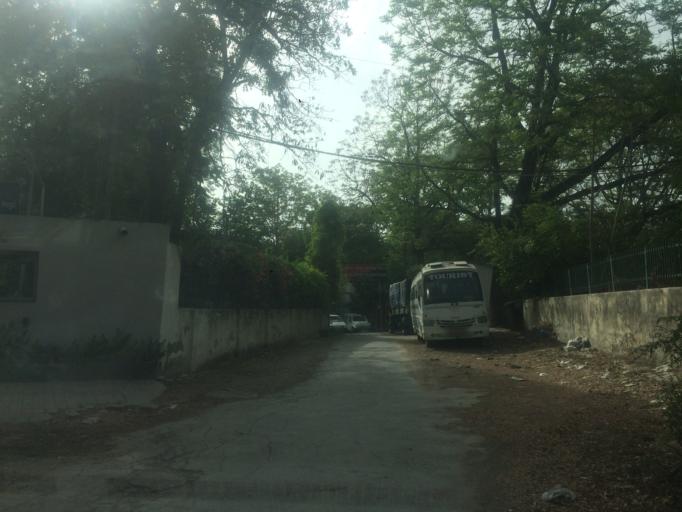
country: IN
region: NCT
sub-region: Central Delhi
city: Karol Bagh
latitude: 28.6349
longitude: 77.1817
